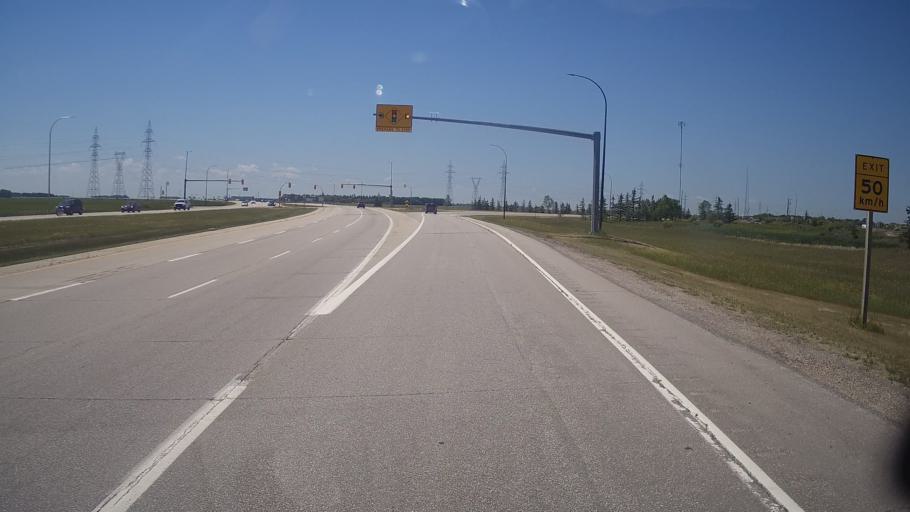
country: CA
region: Manitoba
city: Stonewall
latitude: 49.9885
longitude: -97.3074
